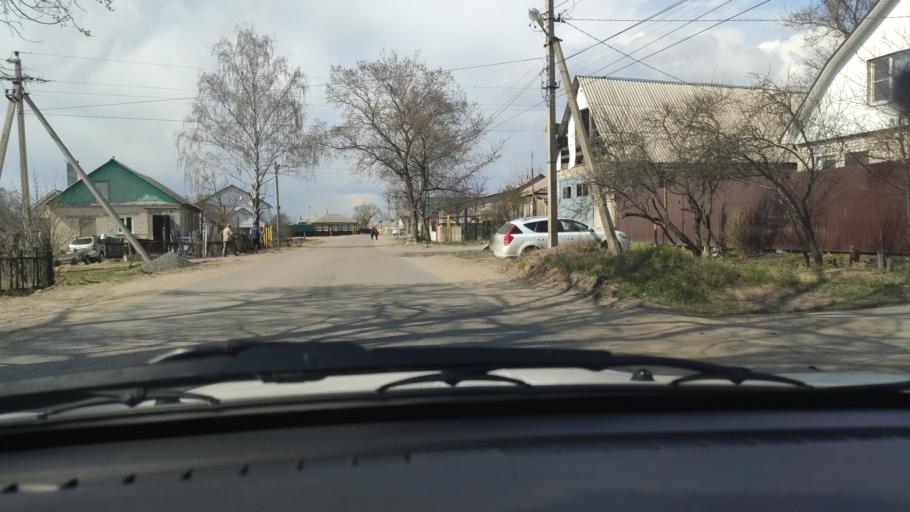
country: RU
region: Voronezj
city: Podgornoye
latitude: 51.7401
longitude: 39.1485
